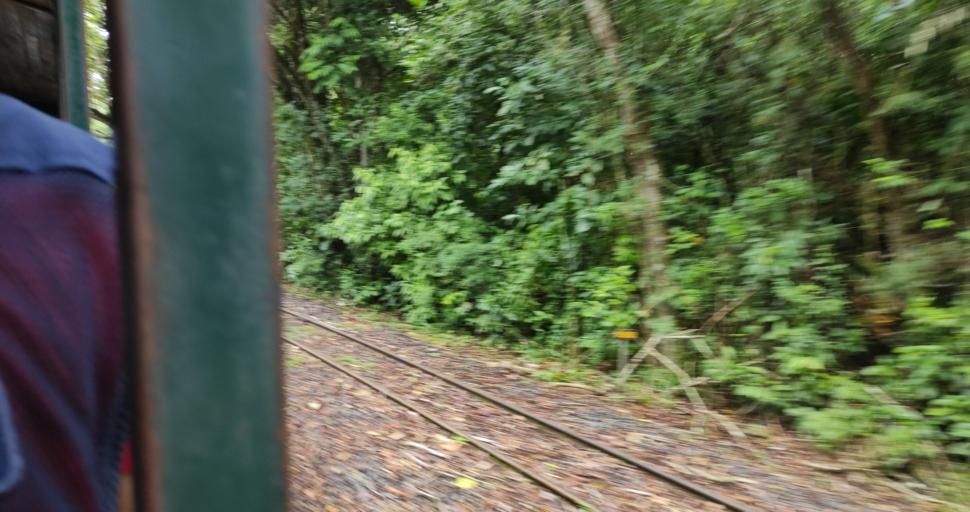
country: AR
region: Misiones
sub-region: Departamento de Iguazu
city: Puerto Iguazu
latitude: -25.6808
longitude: -54.4498
